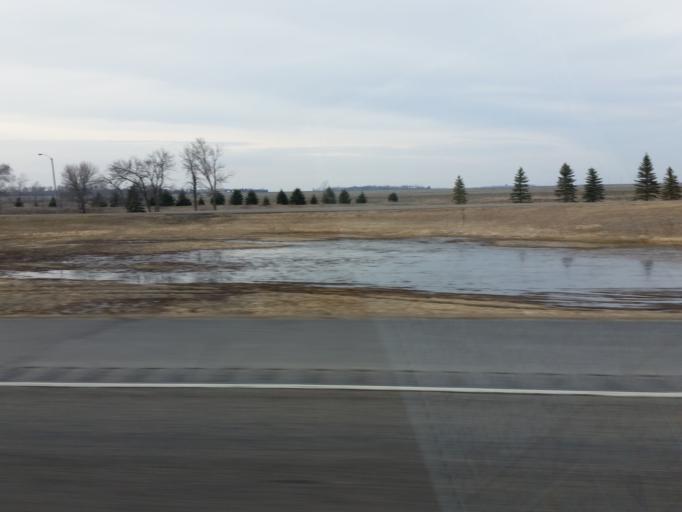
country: US
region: North Dakota
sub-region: Cass County
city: Casselton
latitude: 46.8771
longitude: -97.0867
